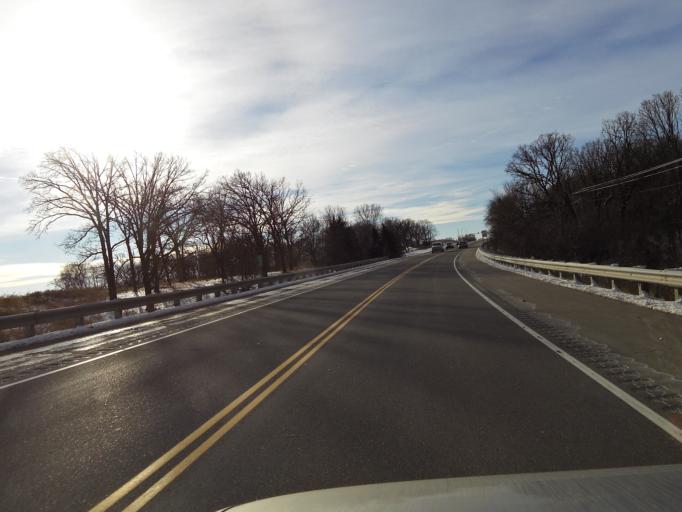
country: US
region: Minnesota
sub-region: Dakota County
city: Rosemount
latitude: 44.7536
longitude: -93.1234
